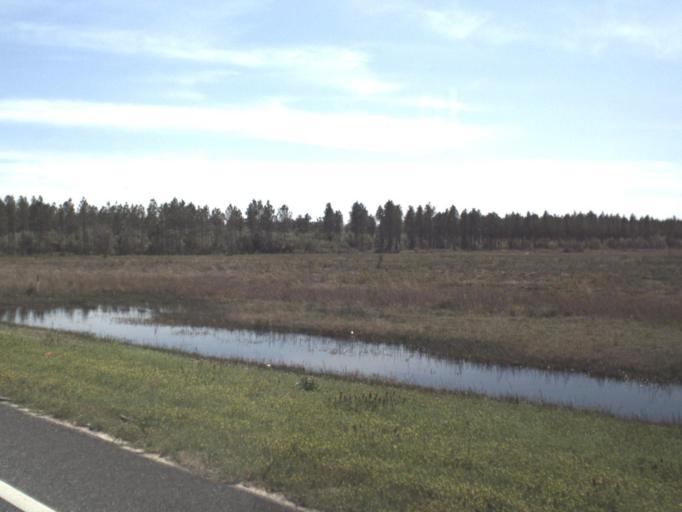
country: US
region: Florida
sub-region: Bay County
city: Lynn Haven
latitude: 30.3554
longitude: -85.6671
